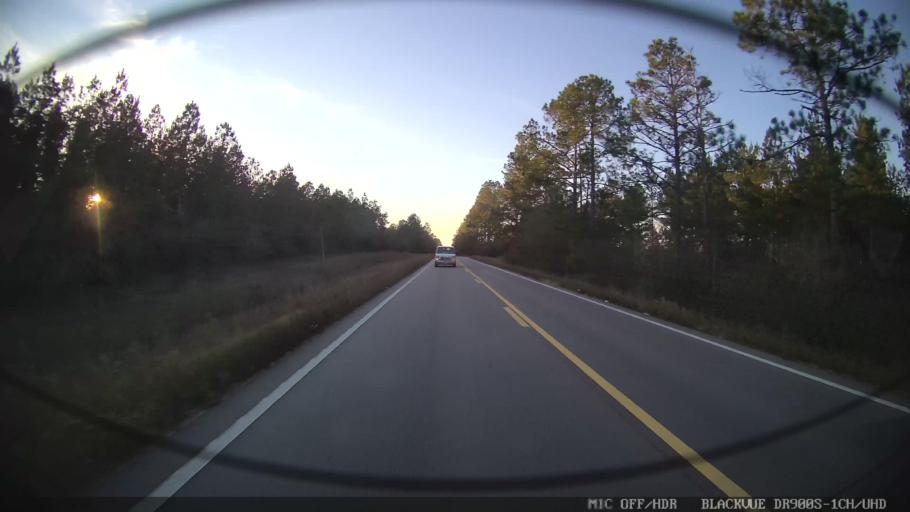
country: US
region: Mississippi
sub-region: Lamar County
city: Lumberton
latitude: 30.9960
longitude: -89.2930
